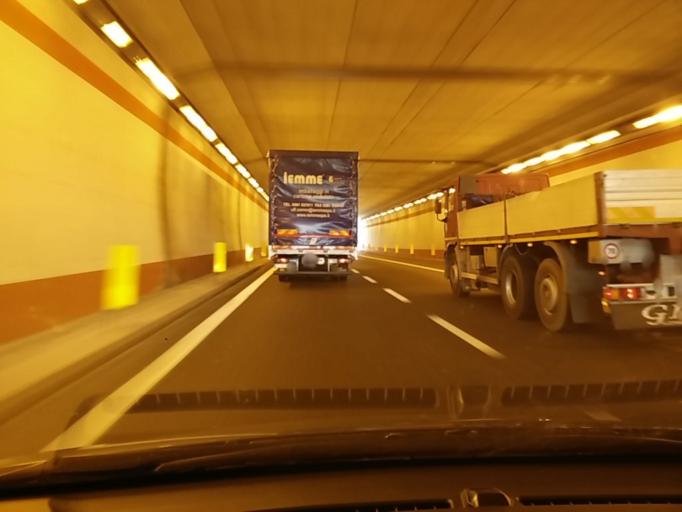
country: IT
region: Lombardy
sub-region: Citta metropolitana di Milano
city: Castano Primo
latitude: 45.5630
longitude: 8.7829
